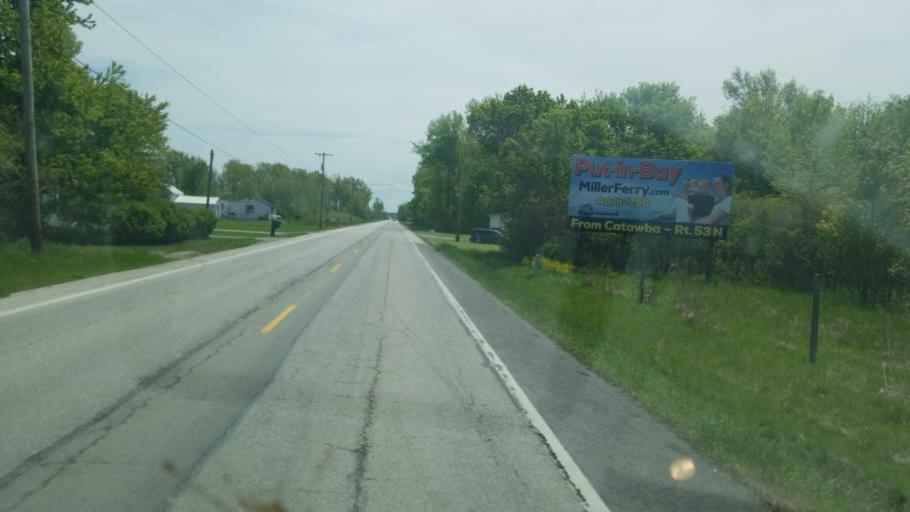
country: US
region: Ohio
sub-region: Ottawa County
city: Oak Harbor
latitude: 41.5528
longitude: -83.0636
